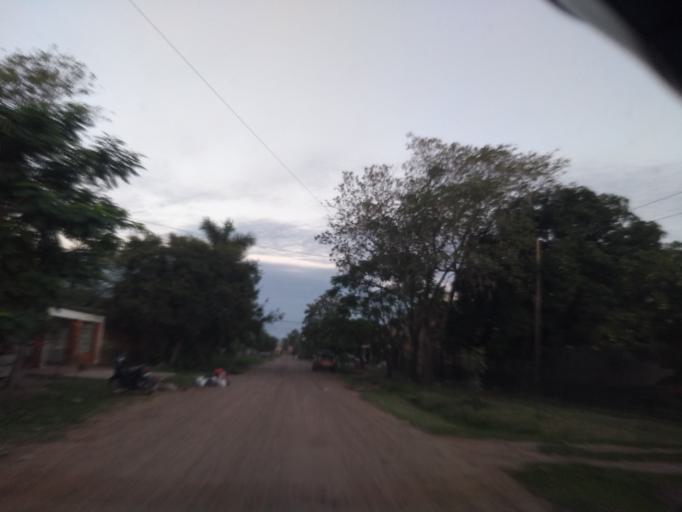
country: AR
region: Chaco
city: Barranqueras
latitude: -27.4845
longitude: -58.9409
